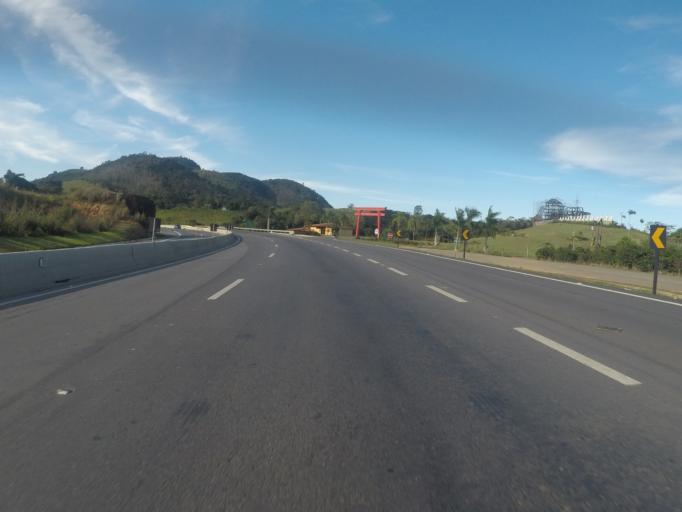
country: BR
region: Espirito Santo
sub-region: Ibiracu
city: Ibiracu
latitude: -19.8656
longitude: -40.3841
